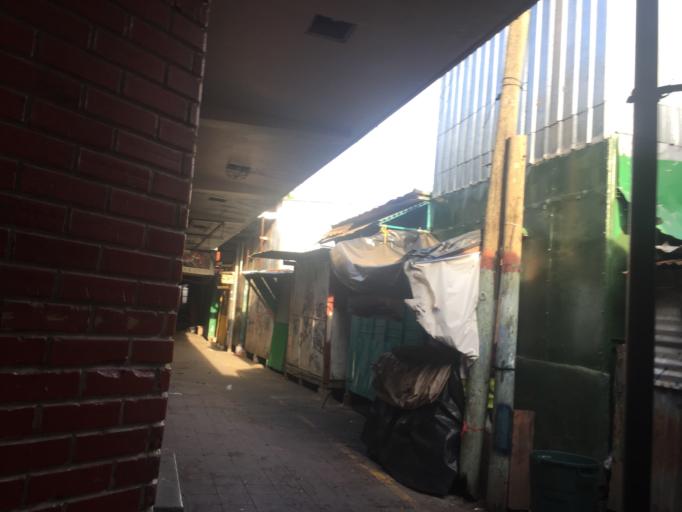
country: NI
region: Managua
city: Managua
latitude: 12.1502
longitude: -86.2594
